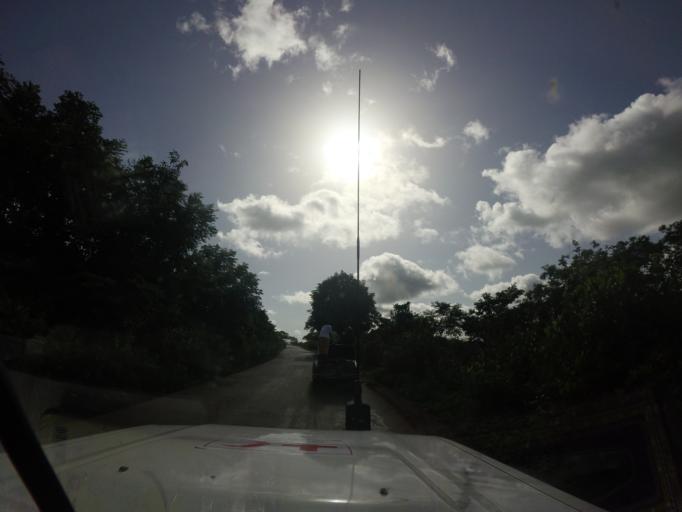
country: GN
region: Mamou
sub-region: Mamou Prefecture
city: Mamou
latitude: 10.2979
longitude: -12.3315
